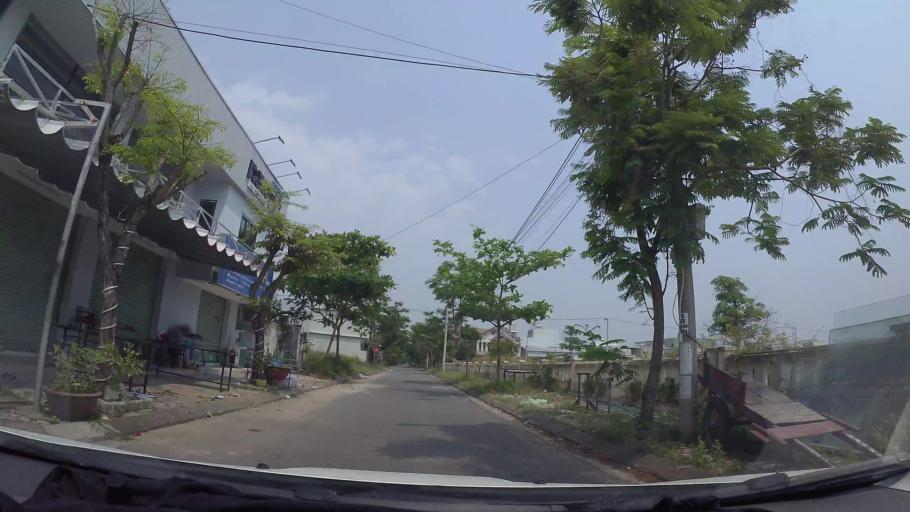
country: VN
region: Da Nang
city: Cam Le
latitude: 15.9981
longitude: 108.2117
